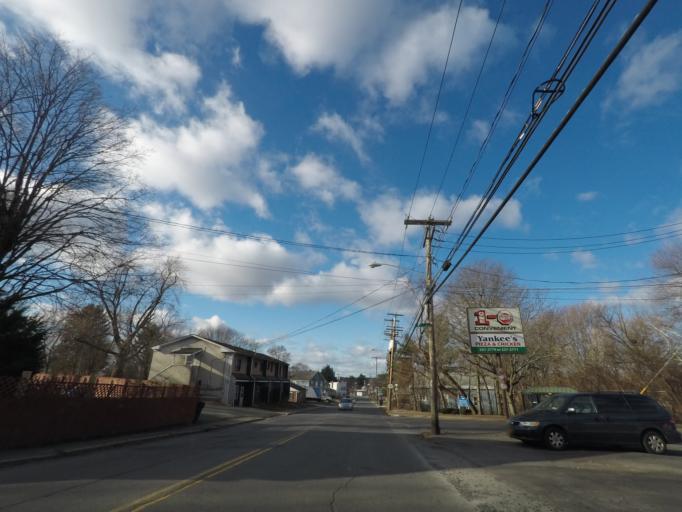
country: US
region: New York
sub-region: Saratoga County
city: Waterford
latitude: 42.7868
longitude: -73.6635
